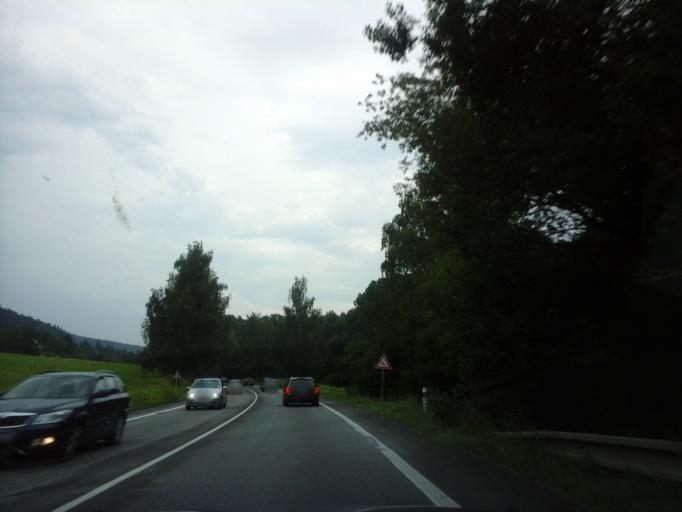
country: CZ
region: South Moravian
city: Cerna Hora
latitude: 49.4055
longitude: 16.5811
